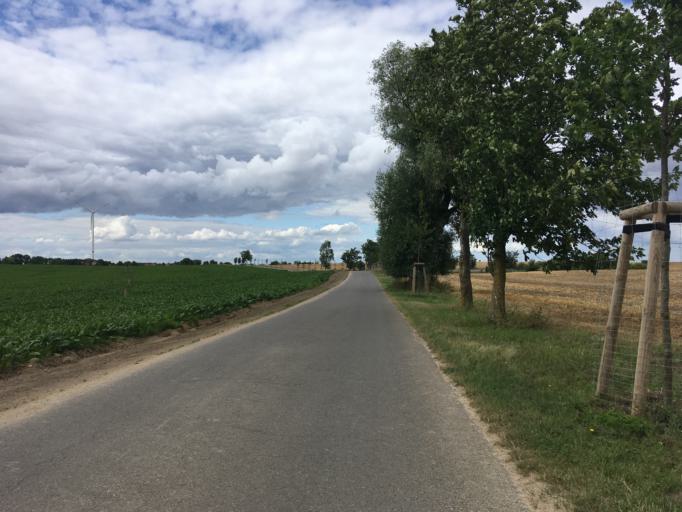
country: DE
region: Brandenburg
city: Gramzow
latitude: 53.2640
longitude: 14.0169
